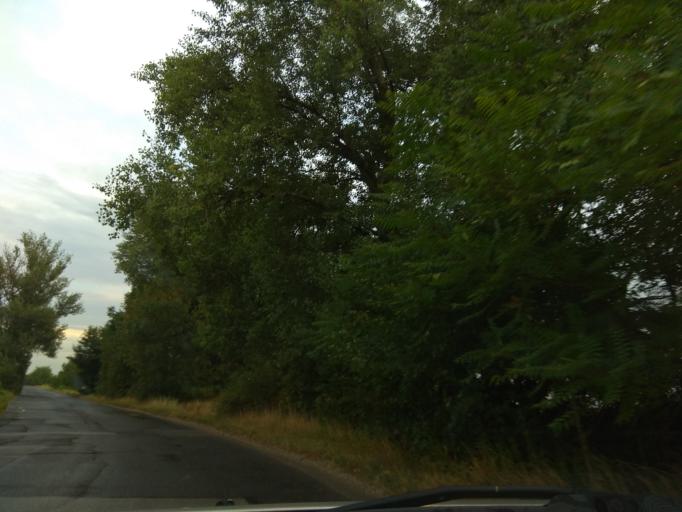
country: HU
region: Borsod-Abauj-Zemplen
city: Felsozsolca
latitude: 48.0957
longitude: 20.8315
